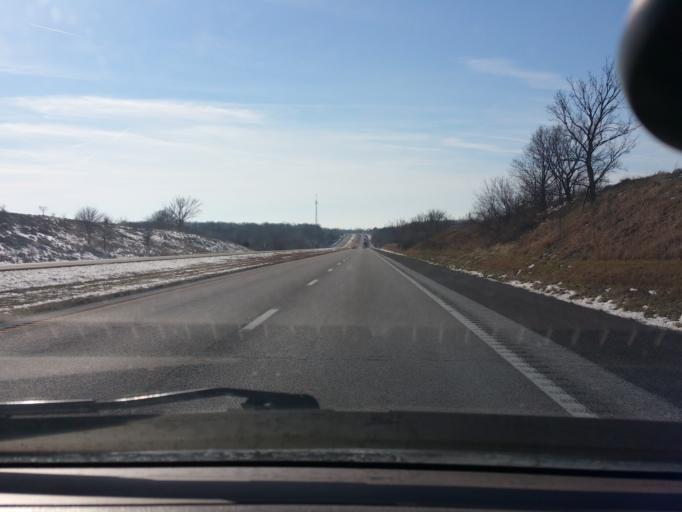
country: US
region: Missouri
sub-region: Clinton County
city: Cameron
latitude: 39.8841
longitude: -94.1606
